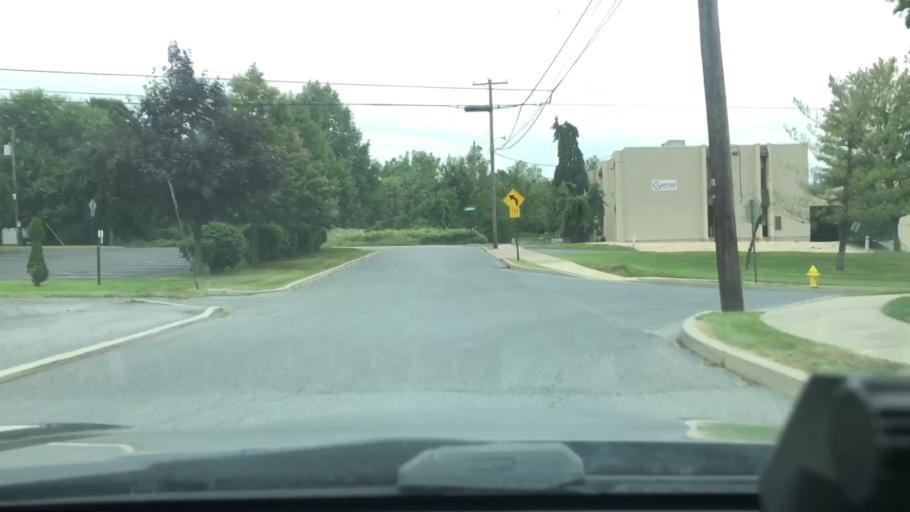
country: US
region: Pennsylvania
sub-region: Lehigh County
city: Fullerton
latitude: 40.6188
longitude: -75.4480
